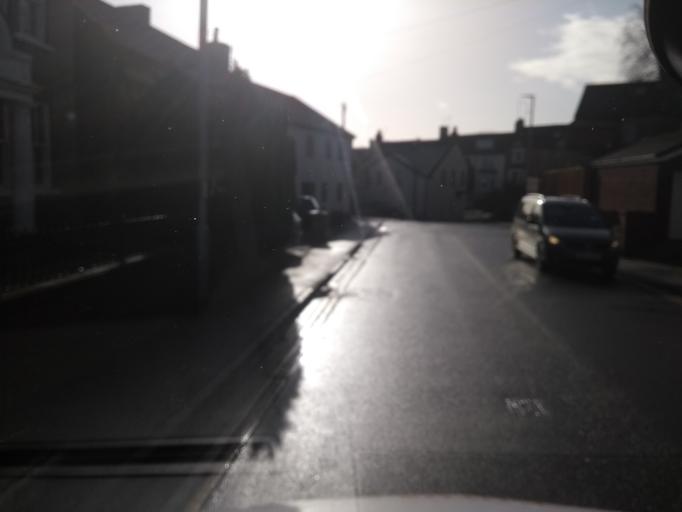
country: GB
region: England
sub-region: Somerset
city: Yeovil
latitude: 50.9455
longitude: -2.6197
